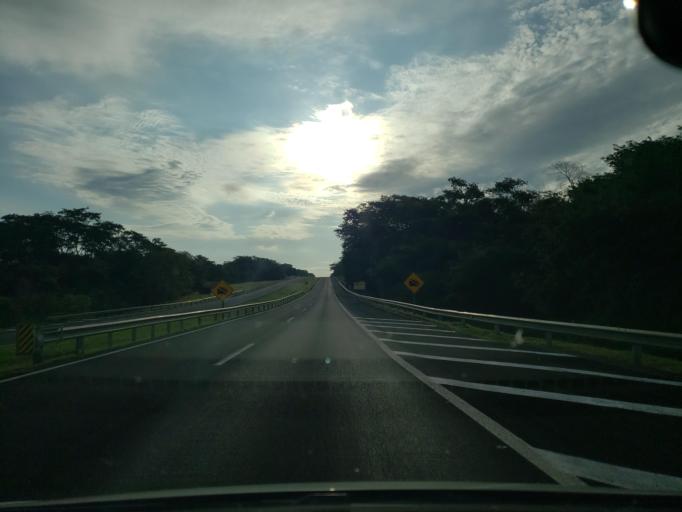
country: BR
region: Sao Paulo
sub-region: Mirandopolis
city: Mirandopolis
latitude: -21.1200
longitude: -51.0091
